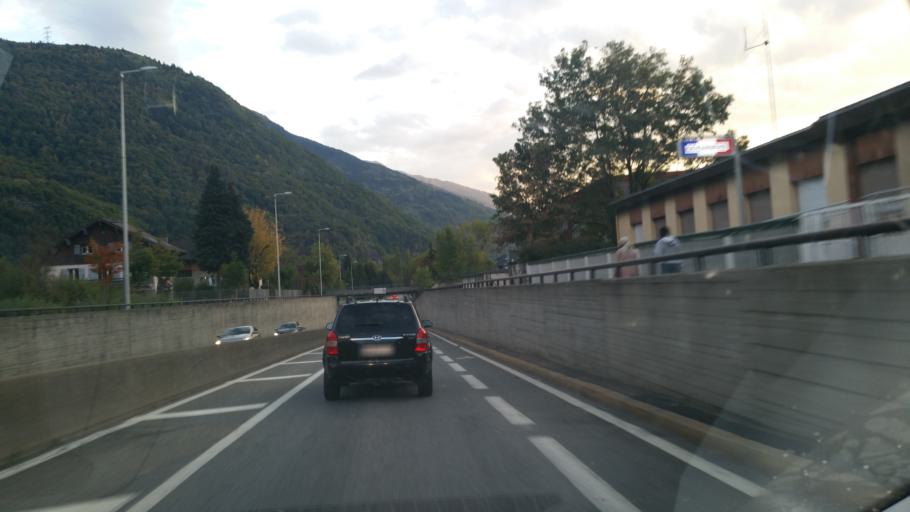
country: FR
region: Rhone-Alpes
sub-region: Departement de la Savoie
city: Albertville
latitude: 45.6676
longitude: 6.3901
